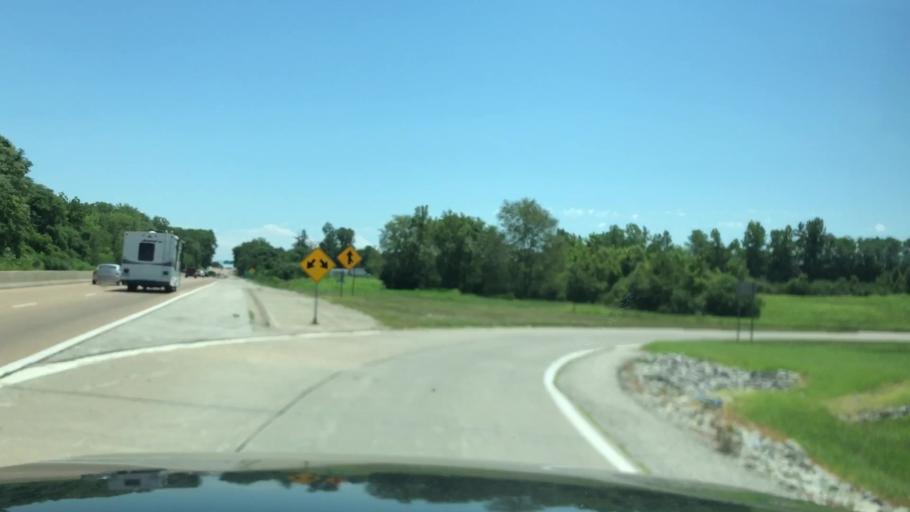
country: US
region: Illinois
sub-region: Saint Clair County
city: Alorton
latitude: 38.5559
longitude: -90.0786
